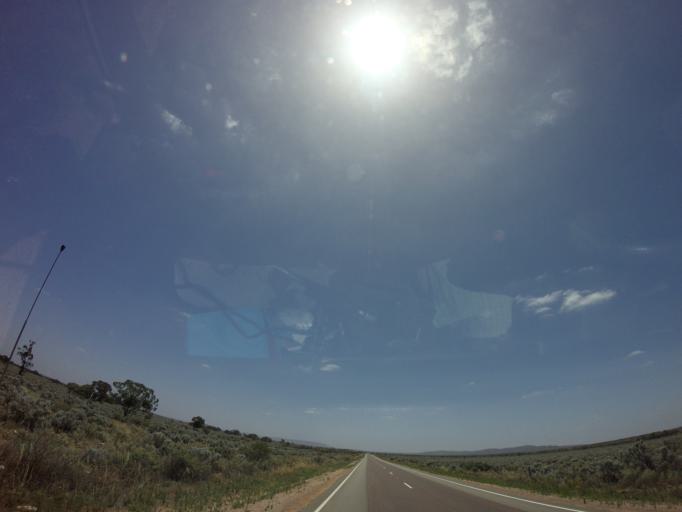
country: AU
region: South Australia
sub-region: Whyalla
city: Whyalla
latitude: -32.8136
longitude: 137.0475
